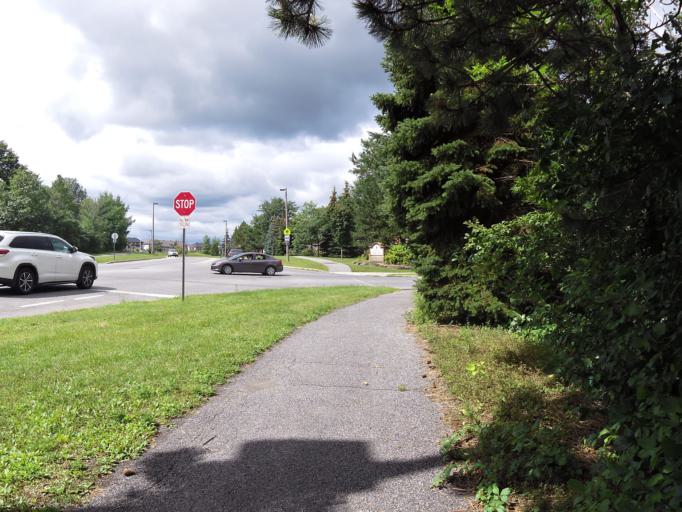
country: CA
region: Ontario
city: Bells Corners
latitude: 45.3238
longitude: -75.9228
